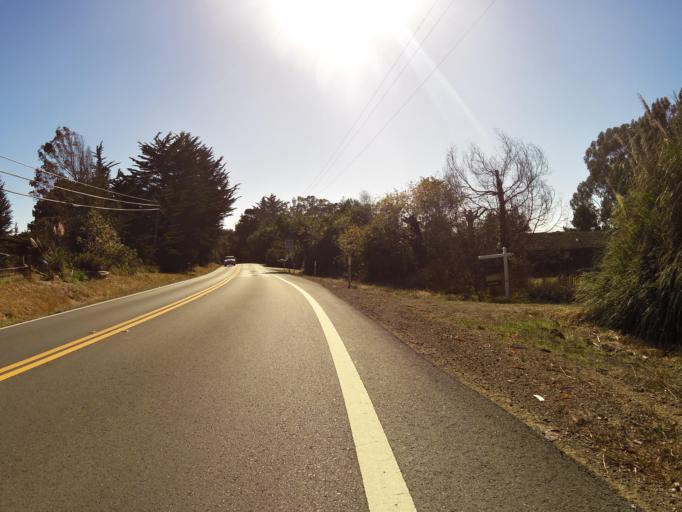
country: US
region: California
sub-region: Mendocino County
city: Fort Bragg
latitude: 39.4984
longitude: -123.7790
